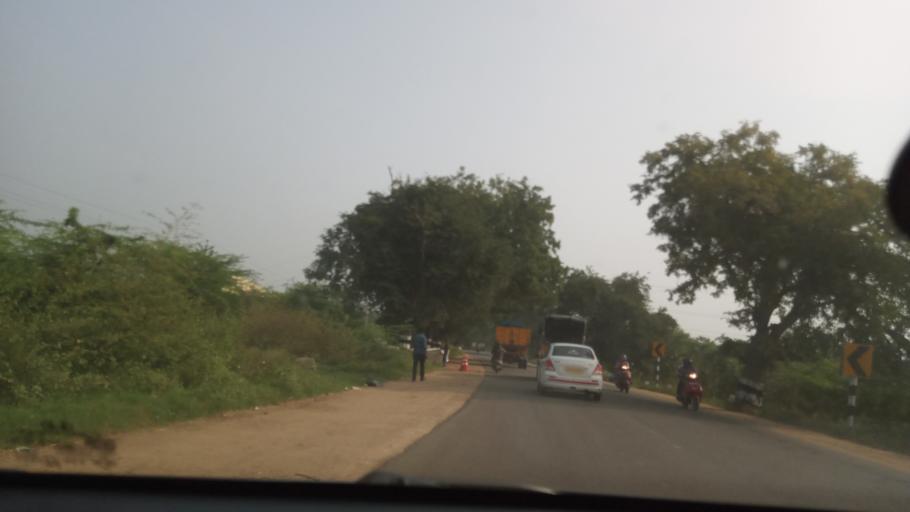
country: IN
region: Tamil Nadu
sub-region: Coimbatore
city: Annur
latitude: 11.1911
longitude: 77.0654
